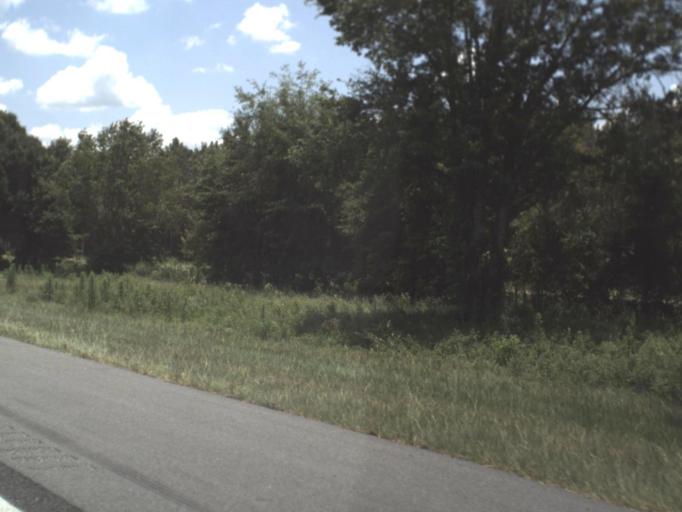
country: US
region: Florida
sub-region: Madison County
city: Madison
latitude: 30.3811
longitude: -83.3041
